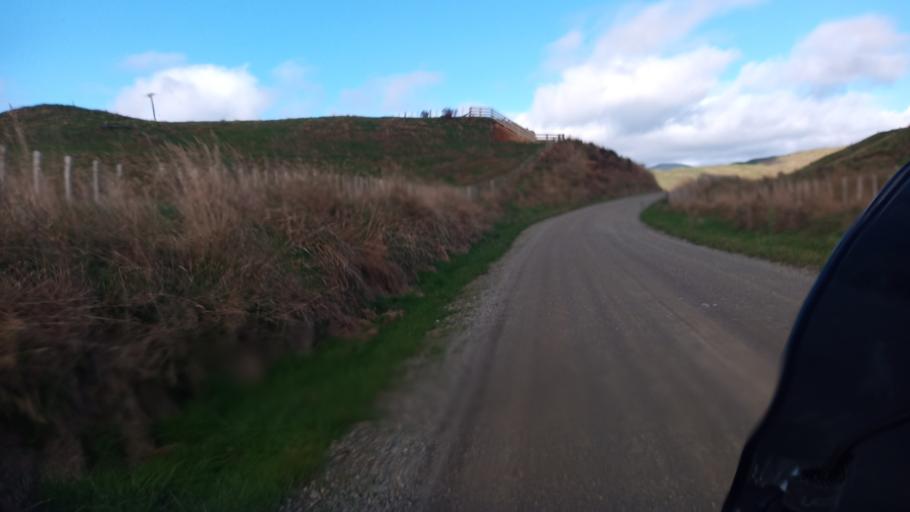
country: NZ
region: Bay of Plenty
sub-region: Opotiki District
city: Opotiki
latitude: -38.4548
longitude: 177.3940
